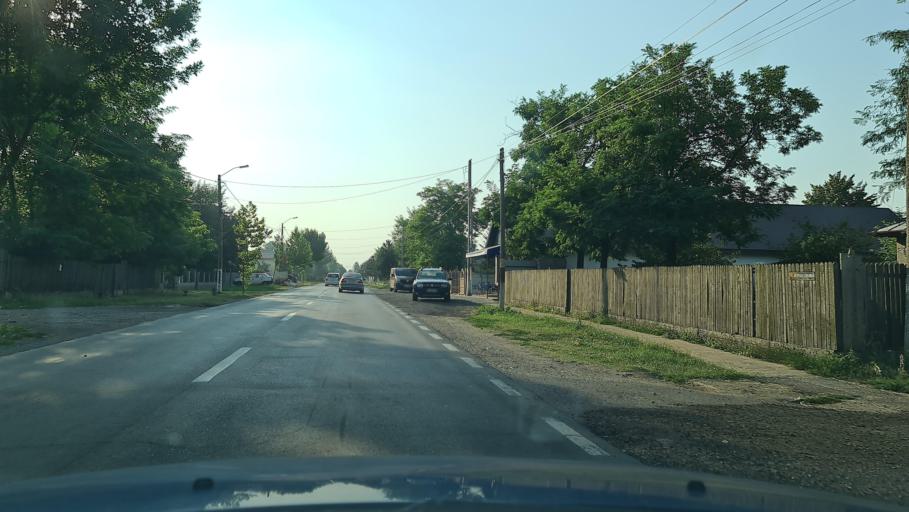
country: RO
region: Calarasi
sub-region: Comuna Dor Marunt
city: Dor Marunt
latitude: 44.4415
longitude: 26.9378
